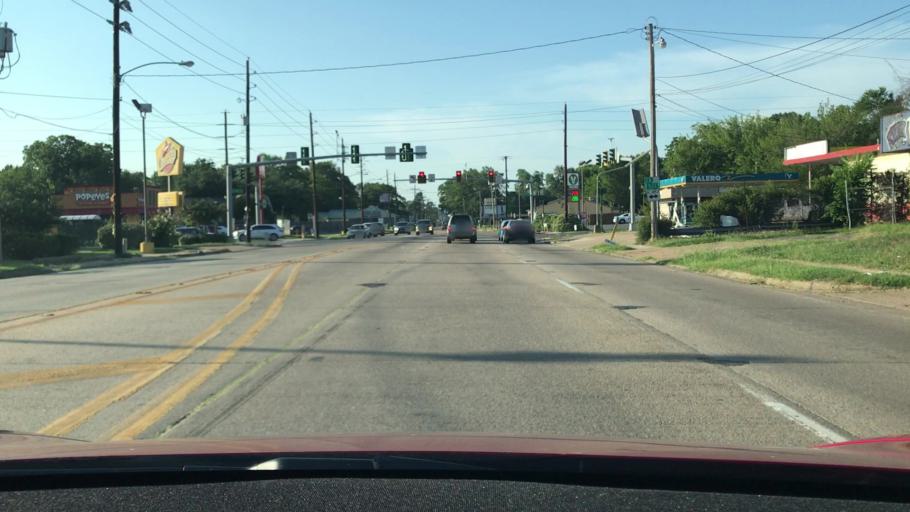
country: US
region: Louisiana
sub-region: Bossier Parish
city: Bossier City
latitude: 32.4414
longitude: -93.7459
